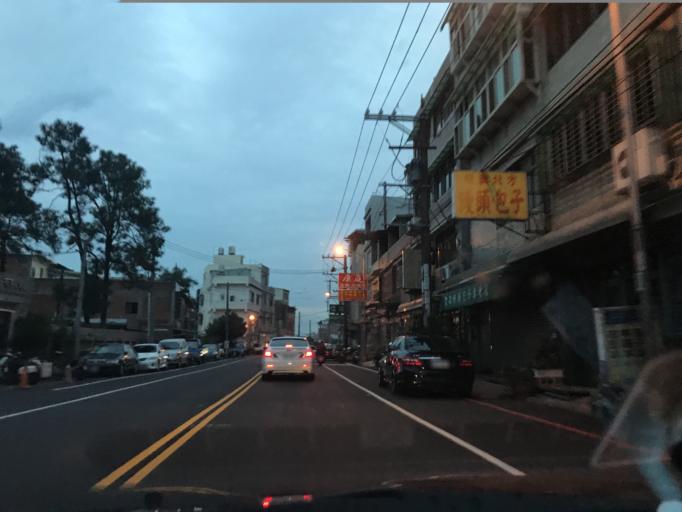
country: TW
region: Taiwan
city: Taoyuan City
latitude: 24.9426
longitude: 121.2434
